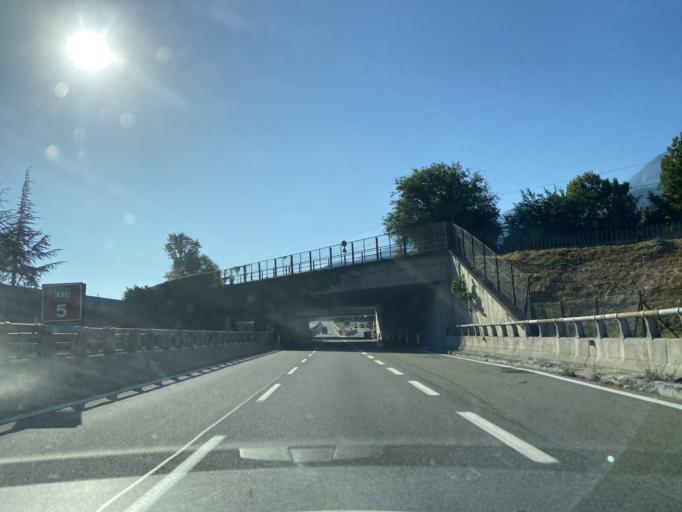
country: IT
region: Piedmont
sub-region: Provincia di Torino
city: Susa
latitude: 45.1382
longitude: 7.0726
